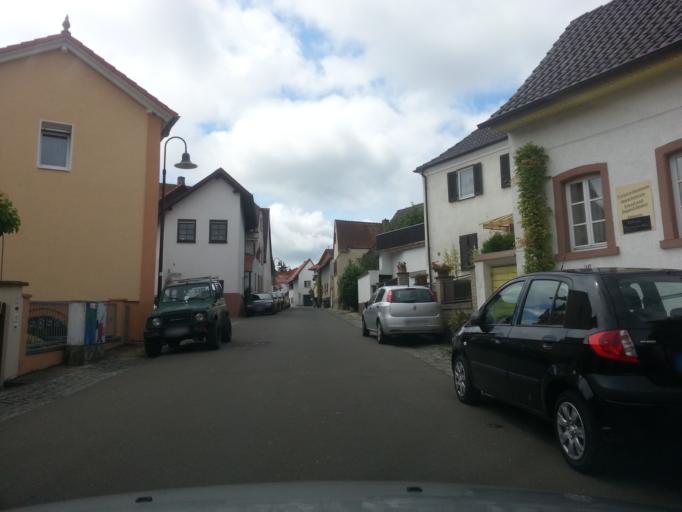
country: DE
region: Rheinland-Pfalz
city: Weisenheim am Berg
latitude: 49.5145
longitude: 8.1513
